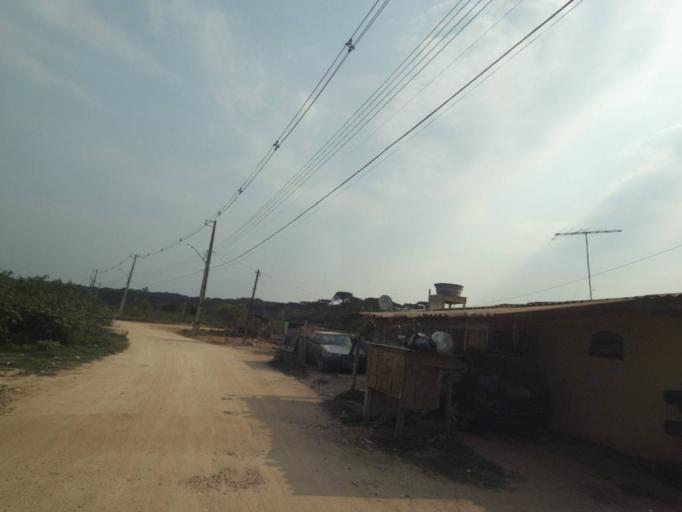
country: BR
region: Parana
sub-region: Sao Jose Dos Pinhais
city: Sao Jose dos Pinhais
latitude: -25.5400
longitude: -49.2321
